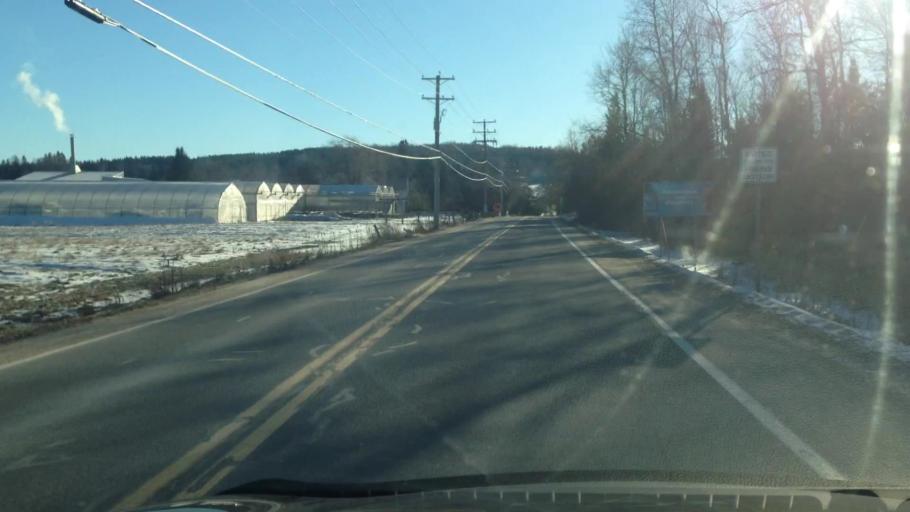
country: CA
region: Quebec
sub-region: Laurentides
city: Mont-Tremblant
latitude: 45.9719
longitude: -74.6151
